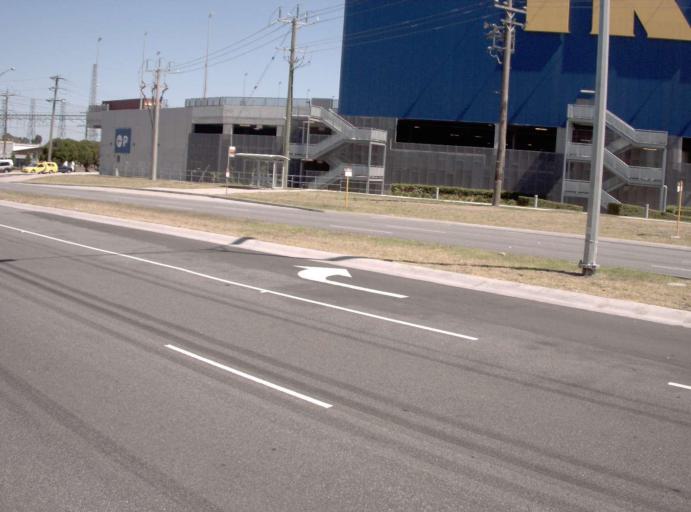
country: AU
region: Victoria
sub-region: Monash
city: Clayton
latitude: -37.9251
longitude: 145.1445
